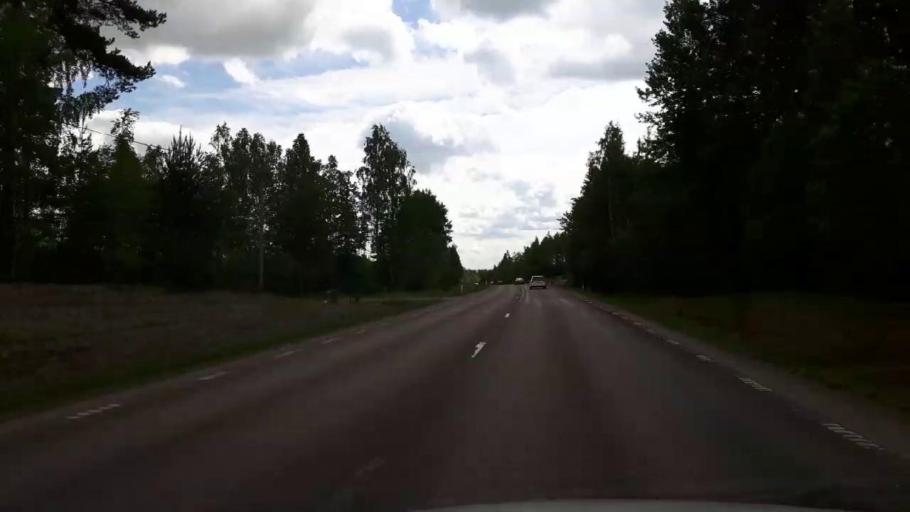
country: SE
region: Dalarna
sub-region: Saters Kommun
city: Saeter
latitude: 60.4663
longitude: 15.7984
